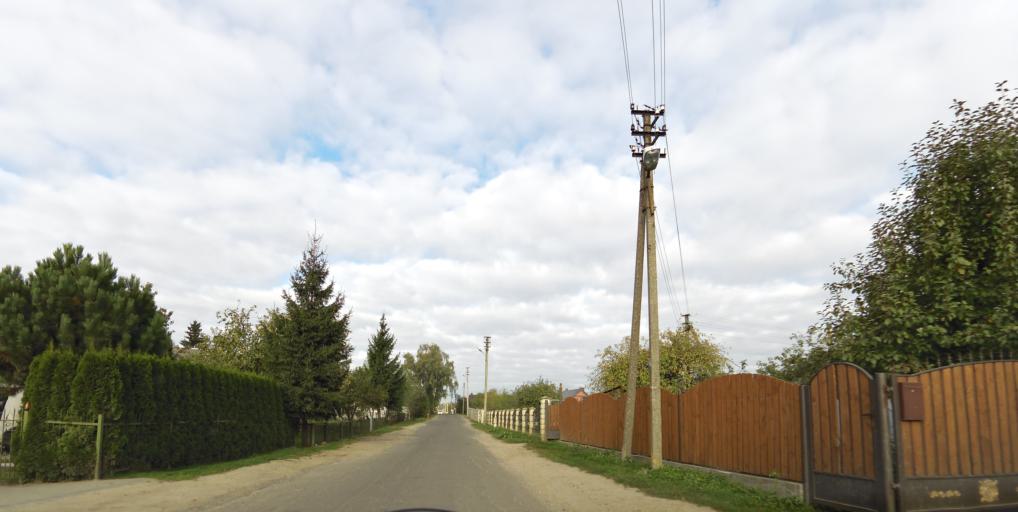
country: LT
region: Vilnius County
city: Pilaite
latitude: 54.7274
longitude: 25.1802
